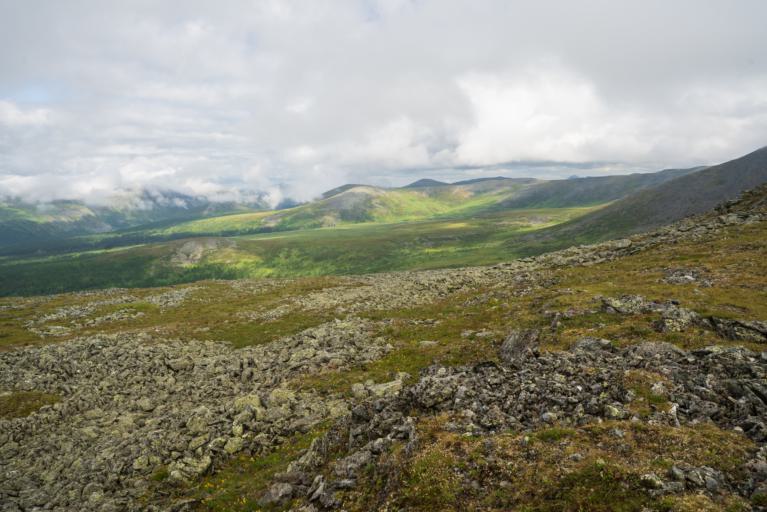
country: RU
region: Komi Republic
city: Synya
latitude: 64.7790
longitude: 59.0502
